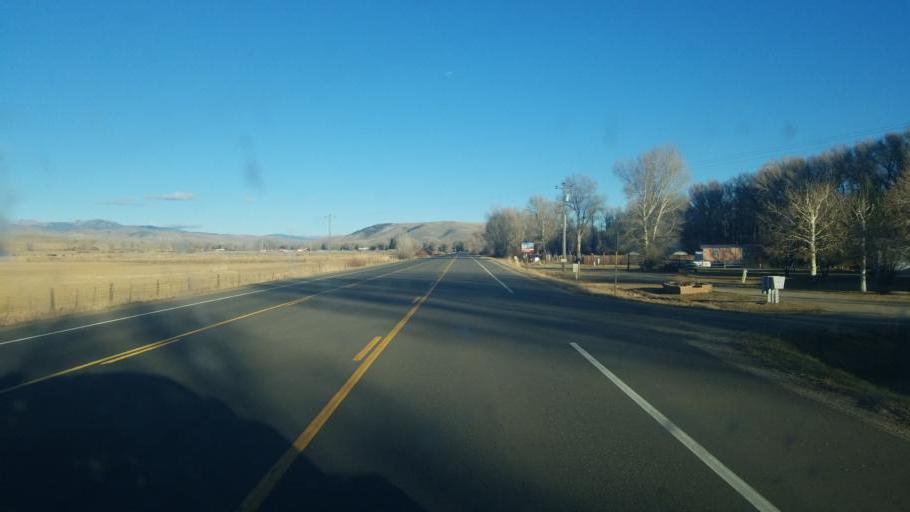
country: US
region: Colorado
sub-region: Gunnison County
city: Gunnison
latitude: 38.5227
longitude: -106.9885
